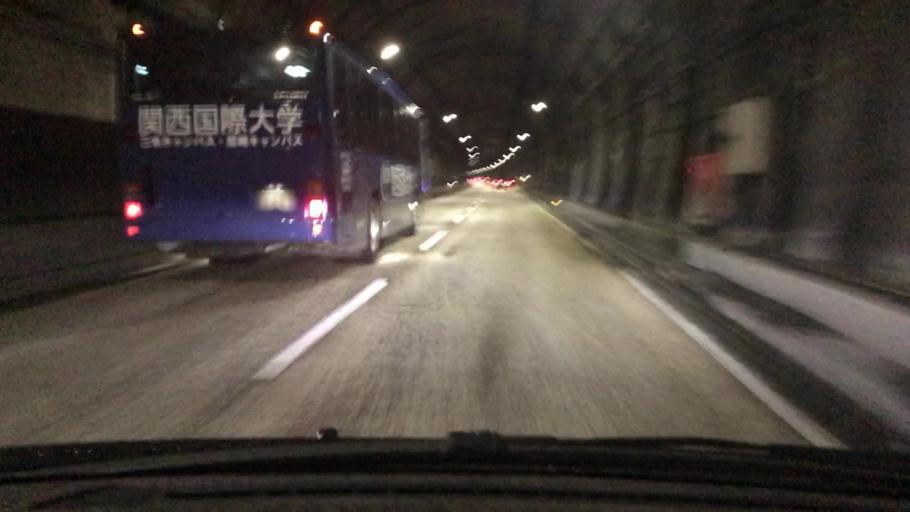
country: JP
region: Hyogo
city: Kobe
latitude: 34.7187
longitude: 135.1872
